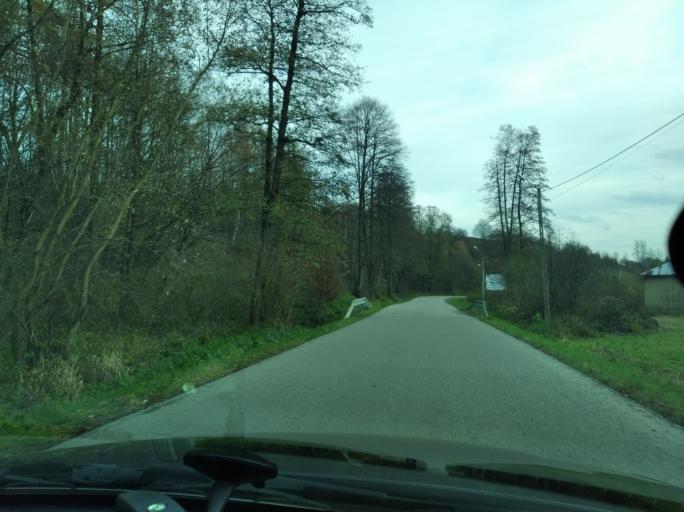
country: PL
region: Subcarpathian Voivodeship
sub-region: Powiat ropczycko-sedziszowski
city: Iwierzyce
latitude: 49.9512
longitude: 21.7266
